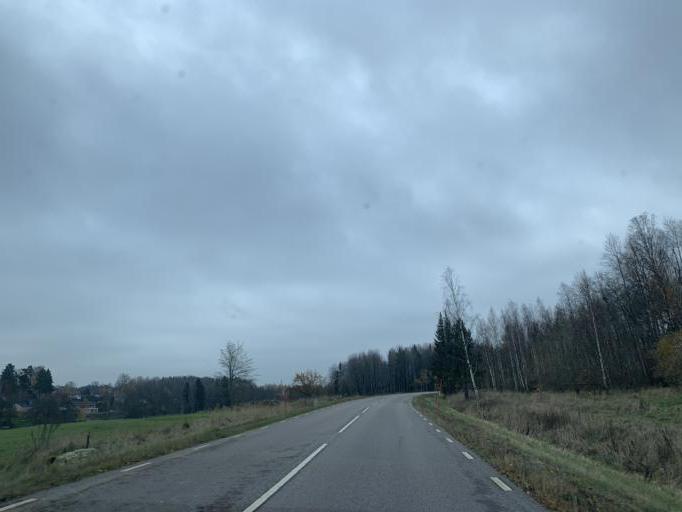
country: SE
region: Vaestmanland
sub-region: Surahammars Kommun
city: Ramnas
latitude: 59.7708
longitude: 16.1909
